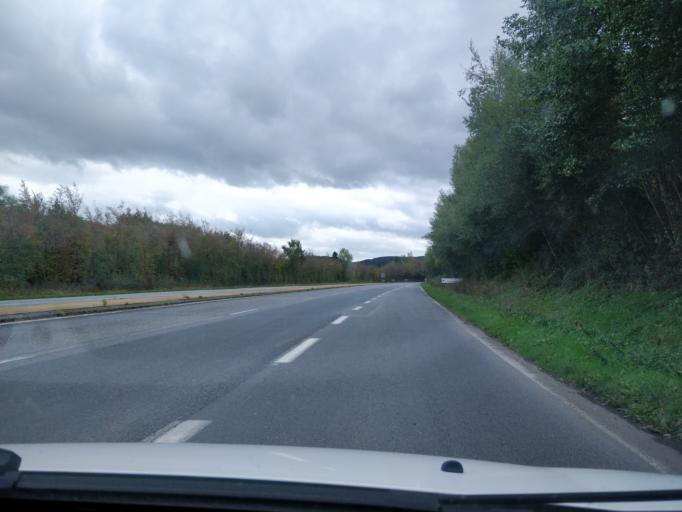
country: FR
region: Lower Normandy
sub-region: Departement de la Manche
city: Villedieu-les-Poeles
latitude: 48.8451
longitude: -1.2013
